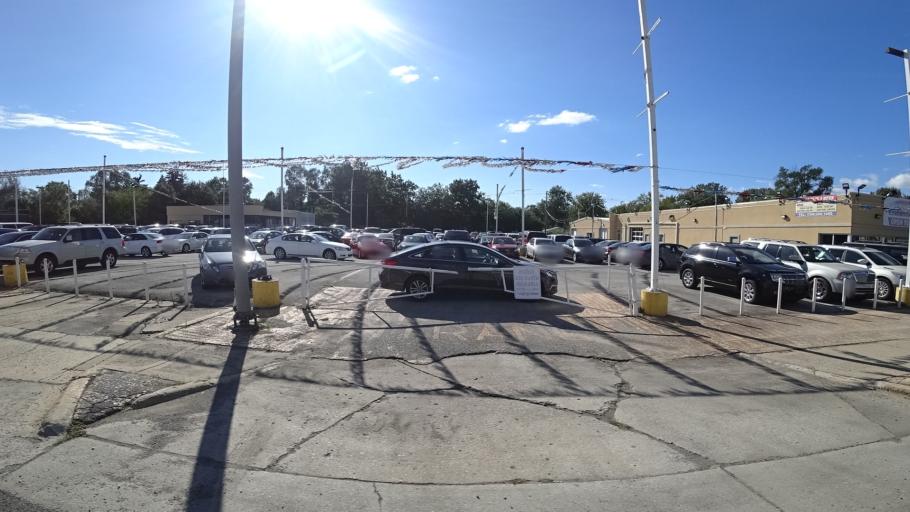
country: US
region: Illinois
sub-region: Cook County
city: Midlothian
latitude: 41.6357
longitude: -87.7378
